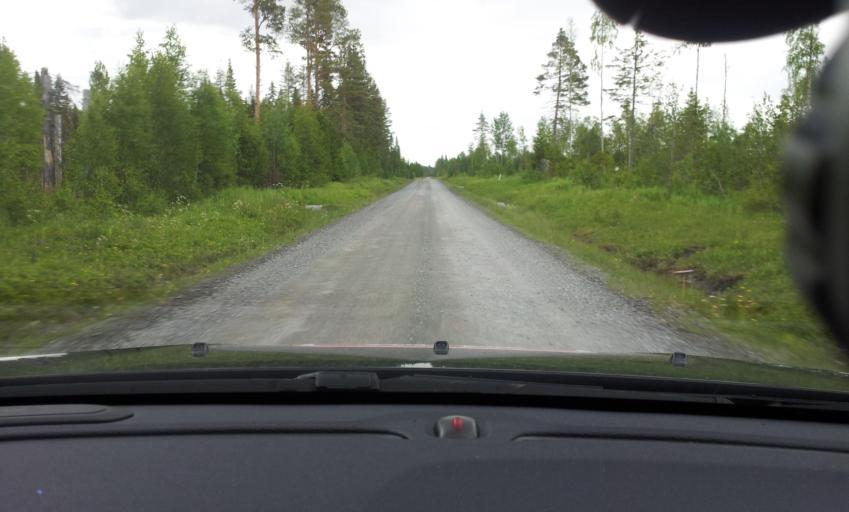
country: SE
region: Jaemtland
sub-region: OEstersunds Kommun
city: Brunflo
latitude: 63.1456
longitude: 15.0433
